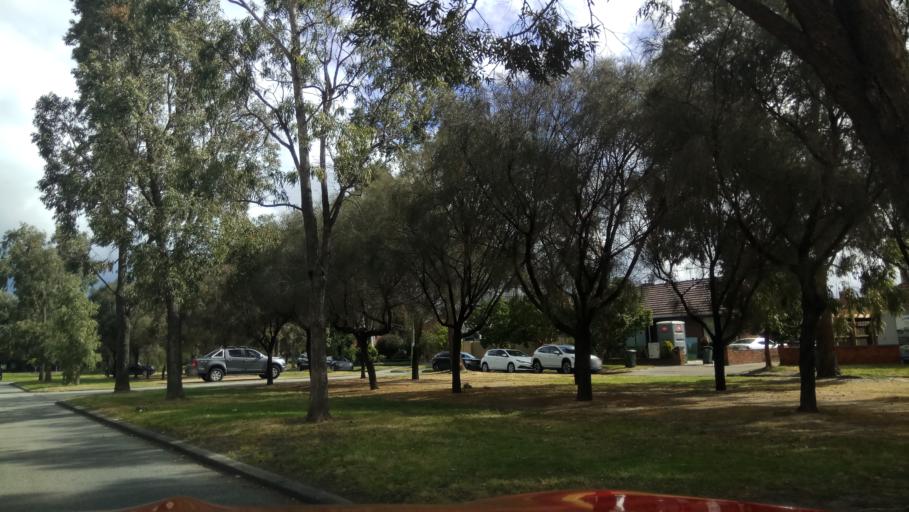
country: AU
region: Victoria
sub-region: Port Phillip
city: Port Melbourne
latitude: -37.8370
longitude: 144.9201
